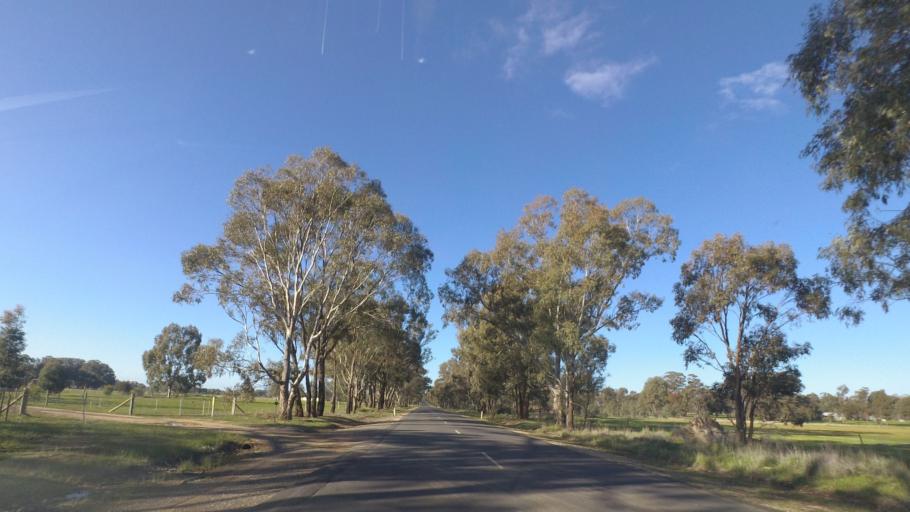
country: AU
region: Victoria
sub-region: Greater Bendigo
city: Epsom
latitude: -36.6602
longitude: 144.4656
